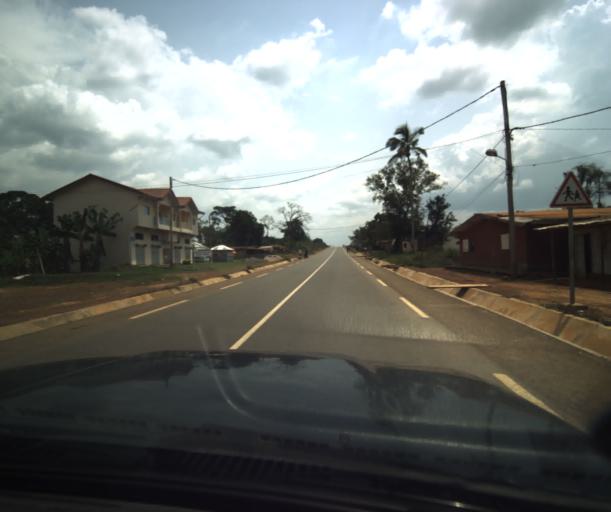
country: CM
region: Centre
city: Akono
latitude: 3.5844
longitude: 11.3039
